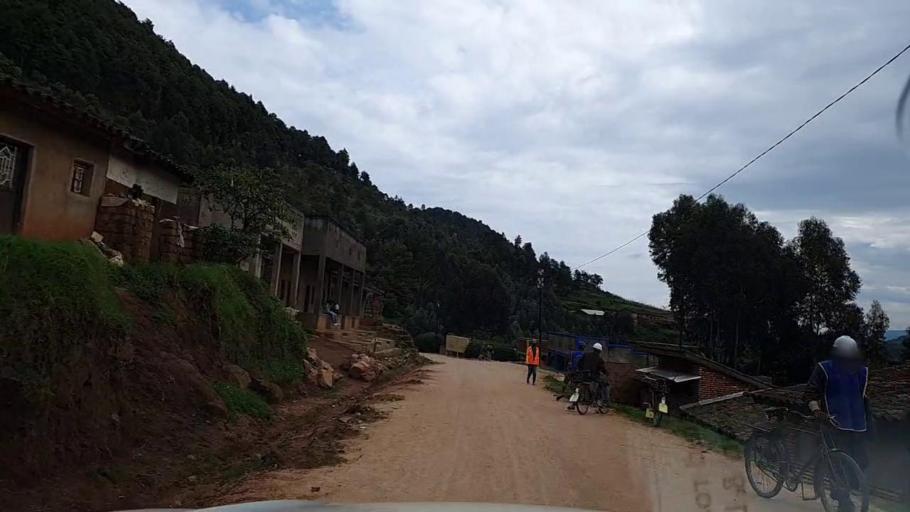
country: RW
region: Southern Province
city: Nzega
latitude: -2.3990
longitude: 29.4538
